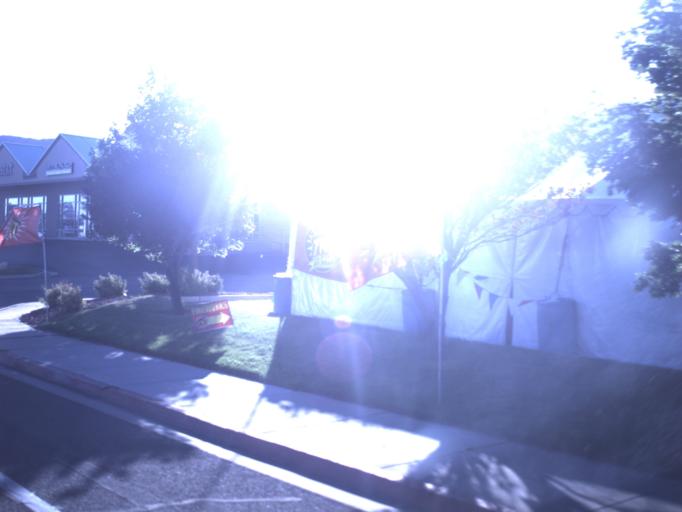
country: US
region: Utah
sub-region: Iron County
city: Cedar City
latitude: 37.6667
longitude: -113.0632
